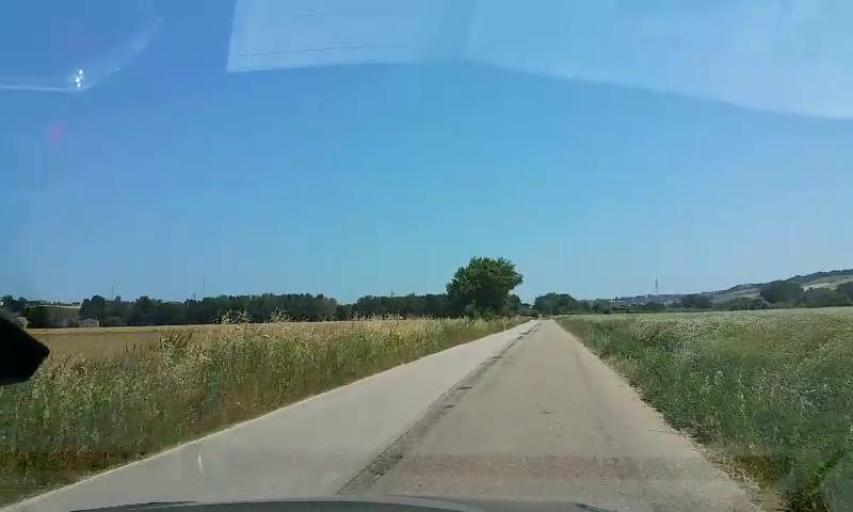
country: IT
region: Molise
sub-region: Provincia di Campobasso
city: San Giacomo degli Schiavoni
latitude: 41.9851
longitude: 14.9303
